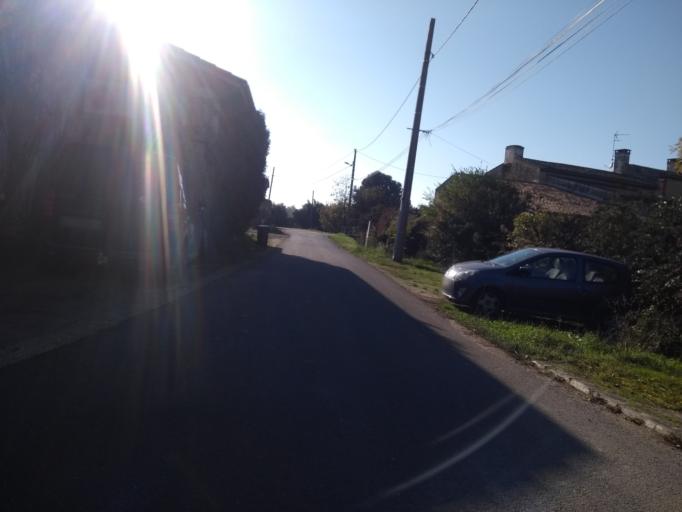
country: FR
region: Aquitaine
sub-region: Departement de la Gironde
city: Cambes
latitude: 44.7229
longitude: -0.4597
